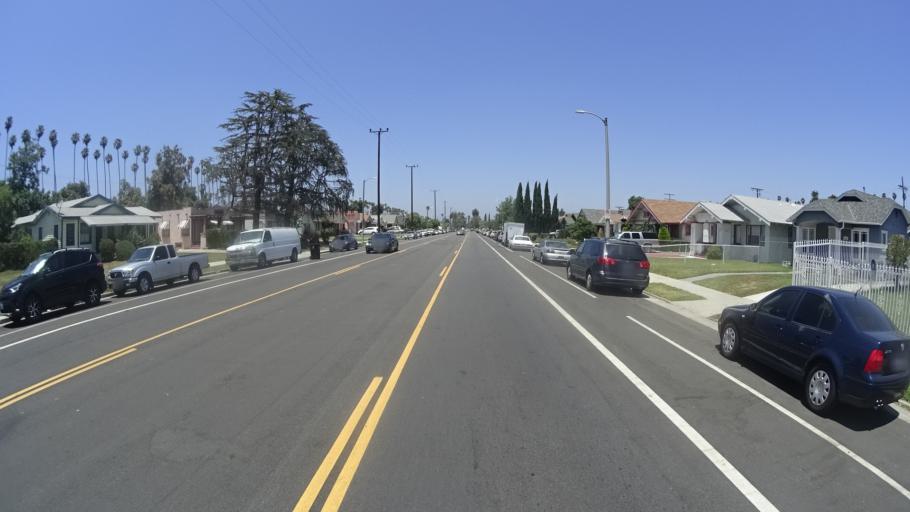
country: US
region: California
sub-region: Los Angeles County
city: View Park-Windsor Hills
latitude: 33.9968
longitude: -118.3192
